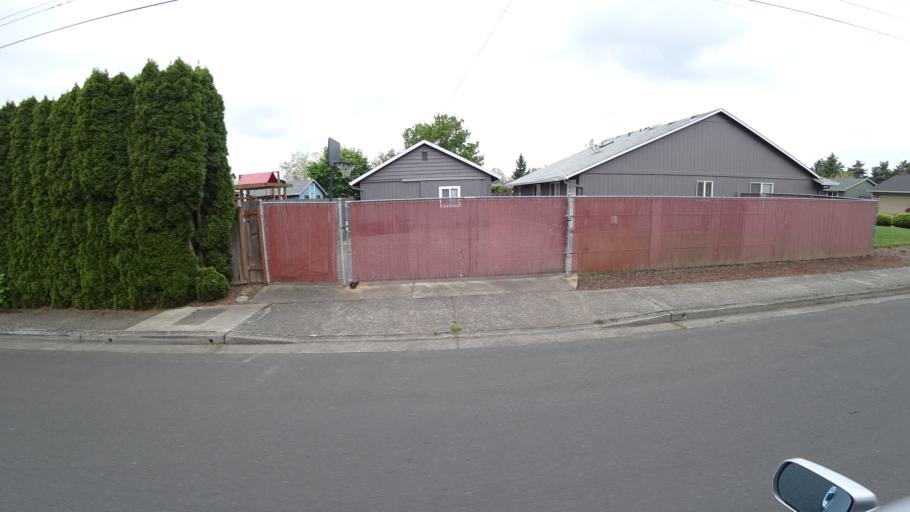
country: US
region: Oregon
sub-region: Washington County
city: Hillsboro
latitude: 45.5399
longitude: -122.9755
